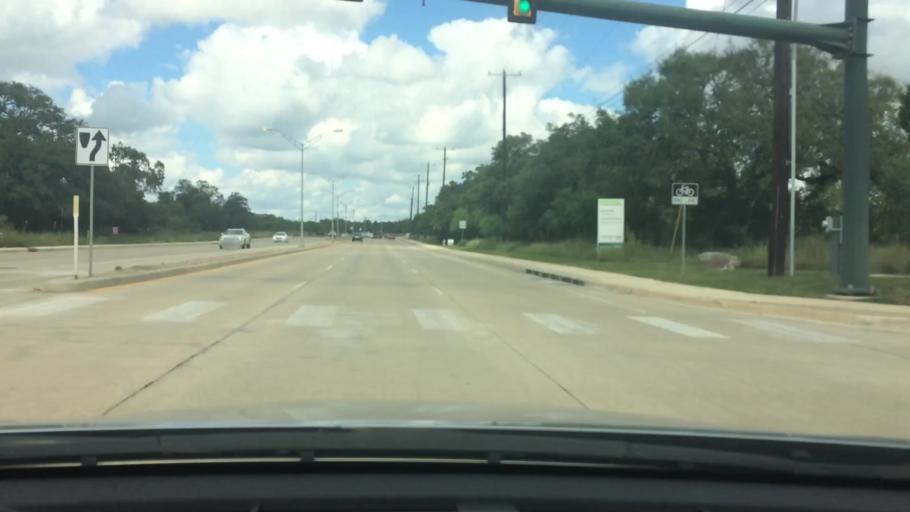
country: US
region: Texas
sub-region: Bexar County
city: Hollywood Park
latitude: 29.6231
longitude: -98.4233
